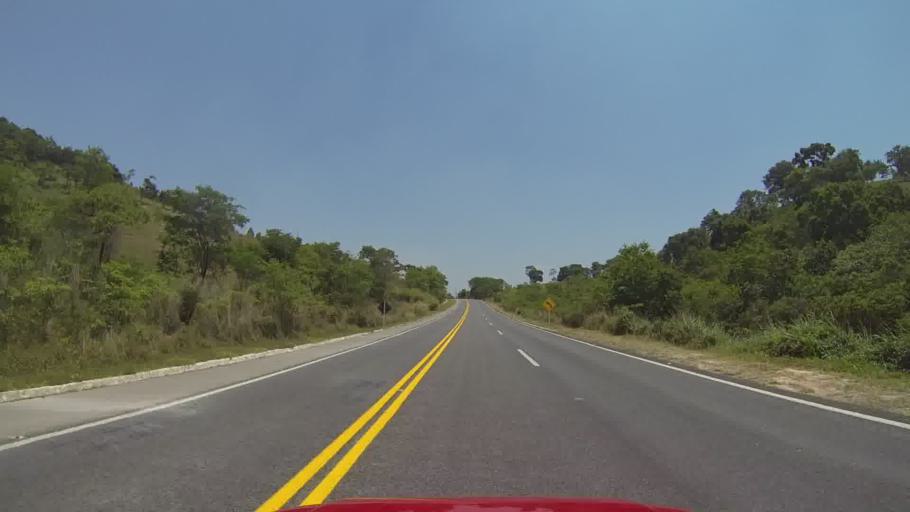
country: BR
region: Minas Gerais
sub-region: Itapecerica
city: Itapecerica
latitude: -20.2937
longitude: -45.1716
